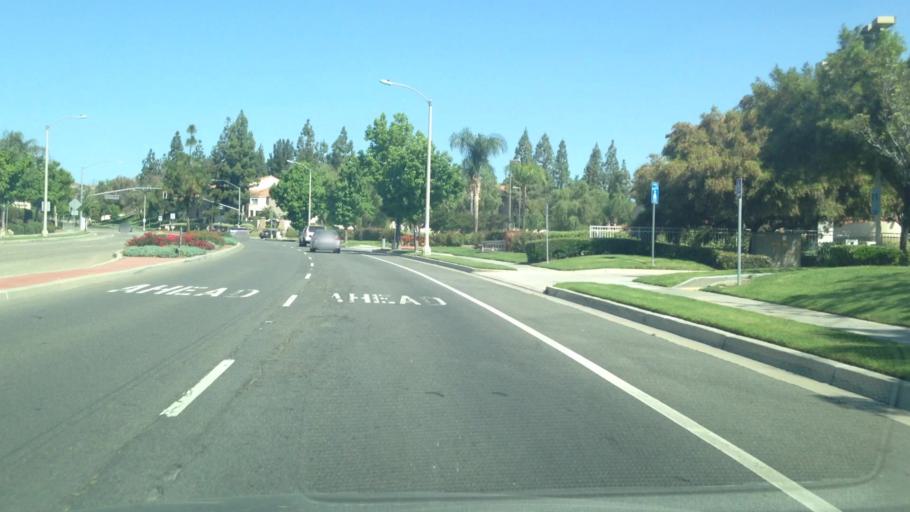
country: US
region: California
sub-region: Riverside County
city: Home Gardens
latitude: 33.8976
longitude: -117.5287
